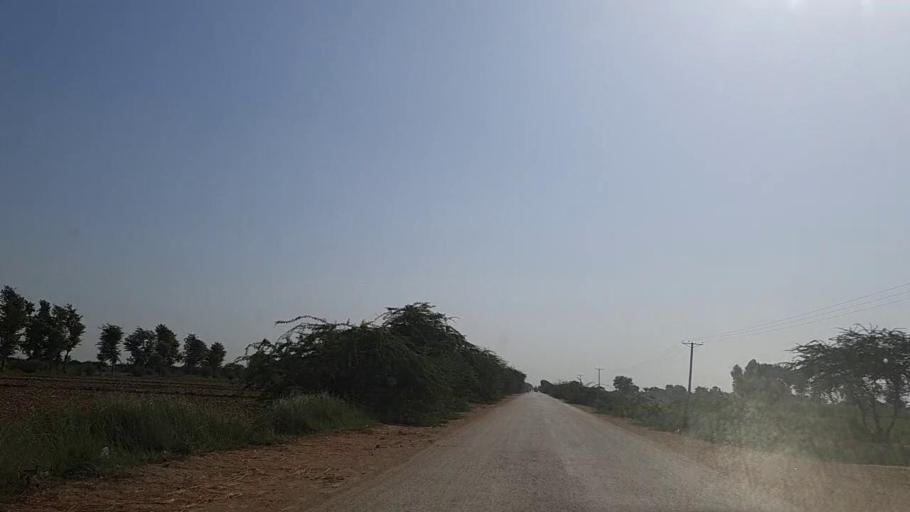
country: PK
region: Sindh
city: Mirpur Batoro
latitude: 24.6017
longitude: 68.2947
